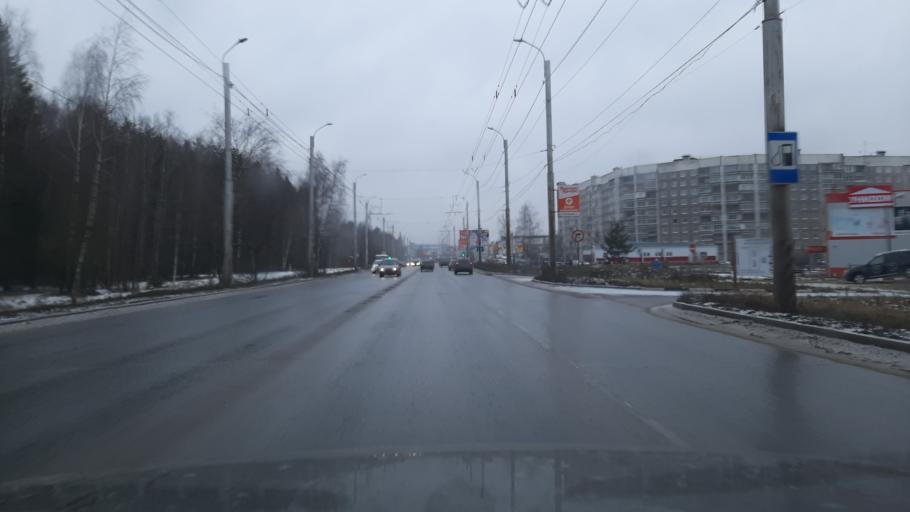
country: RU
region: Ivanovo
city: Kokhma
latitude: 56.9527
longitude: 41.0446
